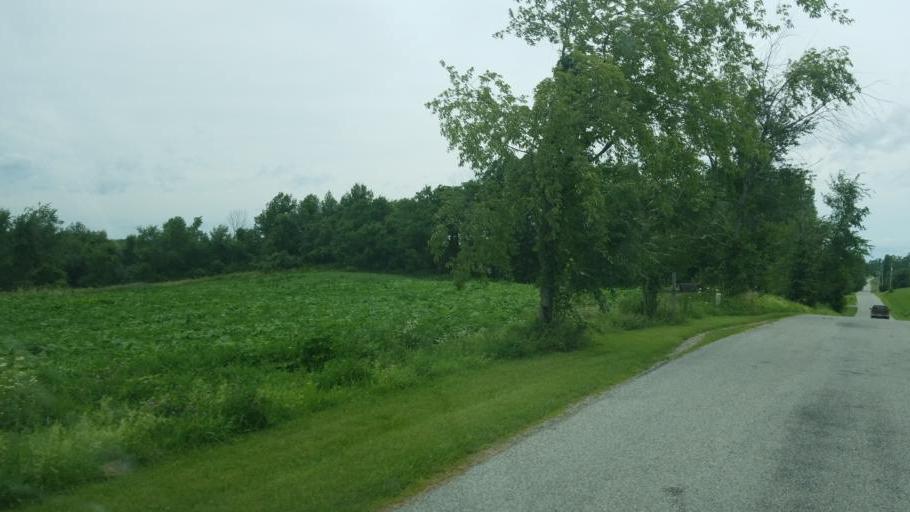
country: US
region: Ohio
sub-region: Licking County
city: Utica
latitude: 40.1951
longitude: -82.5499
